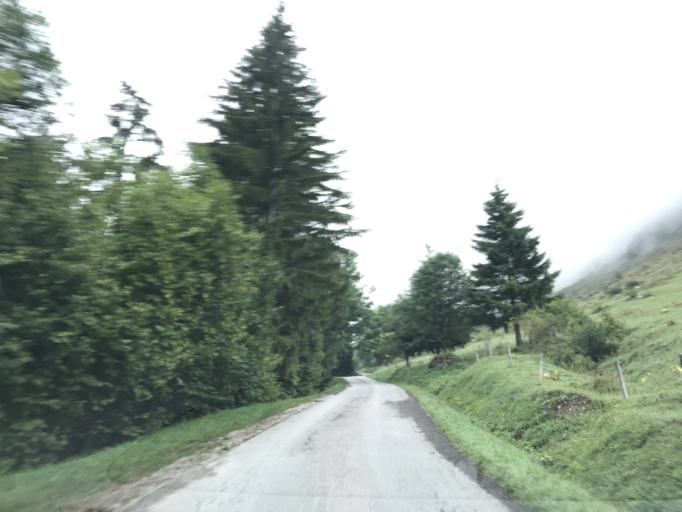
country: FR
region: Rhone-Alpes
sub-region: Departement de la Haute-Savoie
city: Talloires
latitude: 45.8212
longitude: 6.2617
